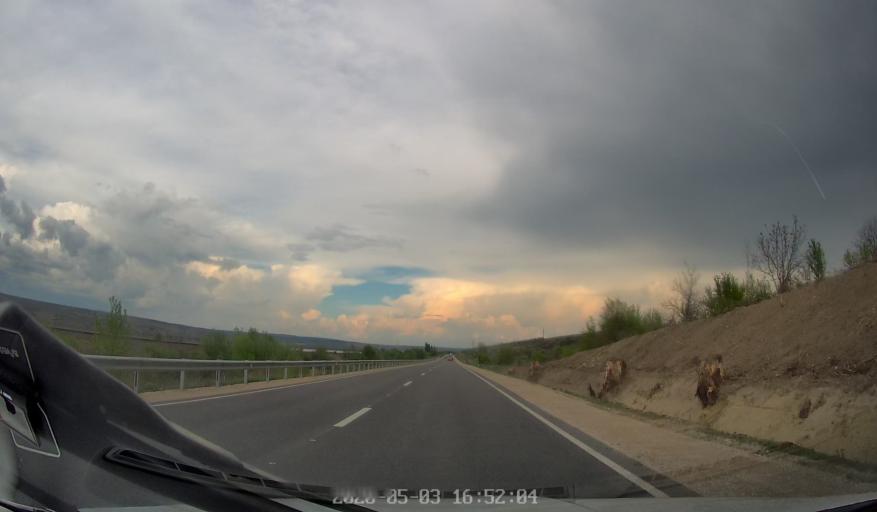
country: MD
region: Straseni
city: Straseni
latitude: 47.1618
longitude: 28.5606
